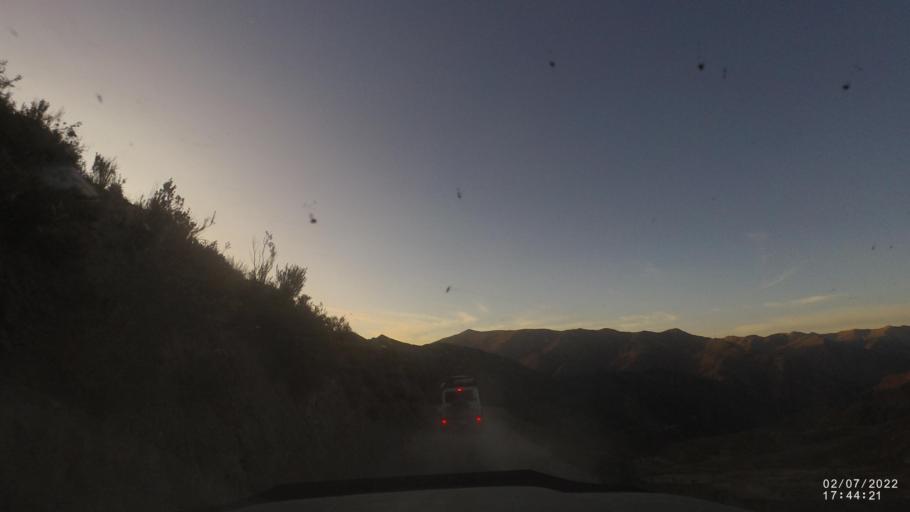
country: BO
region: Cochabamba
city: Irpa Irpa
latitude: -17.8535
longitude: -66.6200
